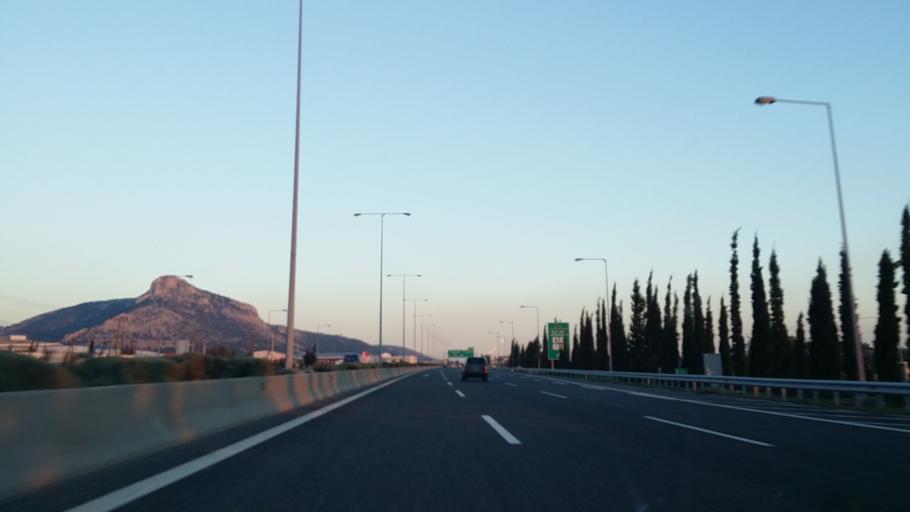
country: GR
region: Attica
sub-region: Nomarchia Dytikis Attikis
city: Aspropyrgos
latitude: 38.0936
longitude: 23.6001
